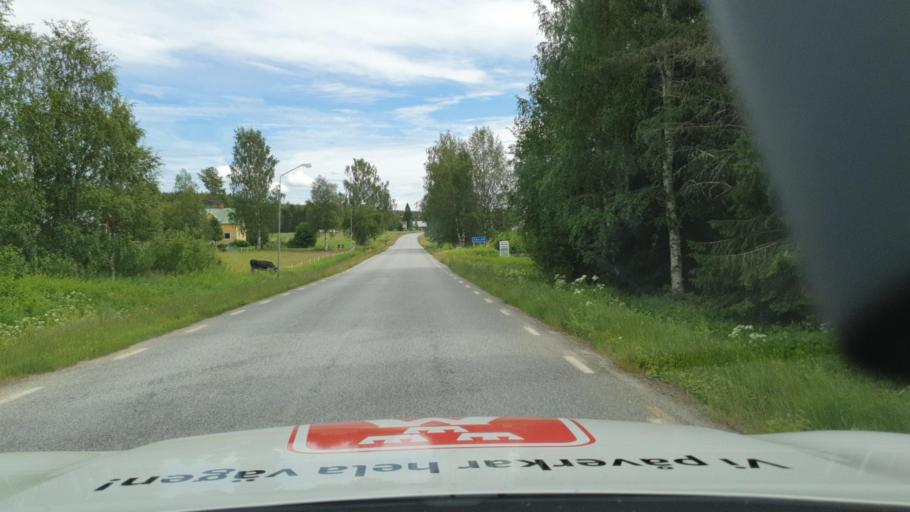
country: SE
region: Vaesterbotten
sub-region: Skelleftea Kommun
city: Soedra Bergsbyn
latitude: 64.5085
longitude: 21.0035
